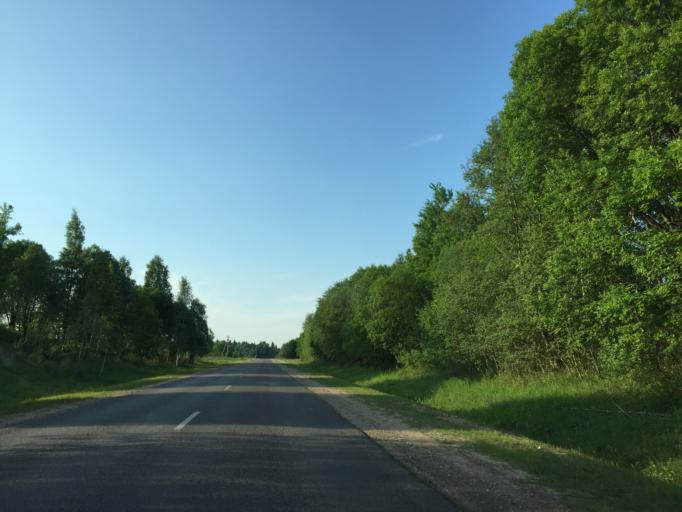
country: LT
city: Plateliai
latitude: 56.0550
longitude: 21.8195
